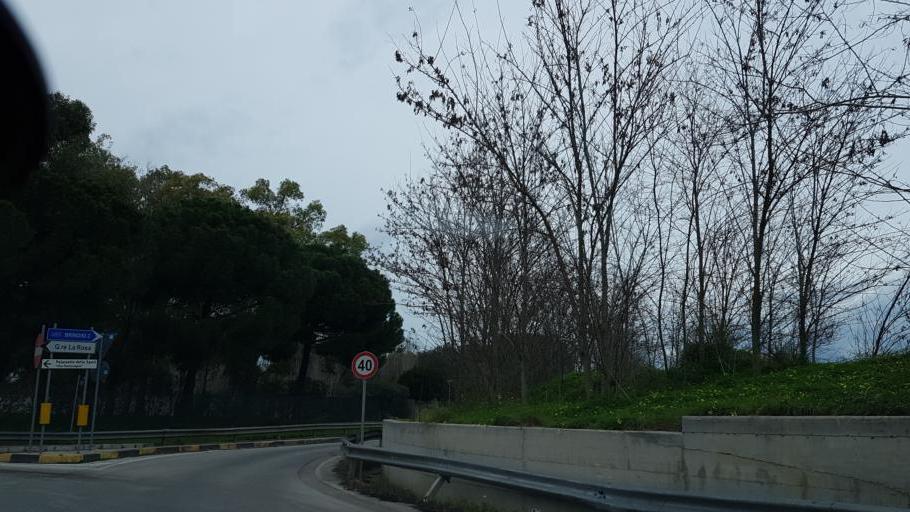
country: IT
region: Apulia
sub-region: Provincia di Brindisi
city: La Rosa
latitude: 40.6096
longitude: 17.9540
